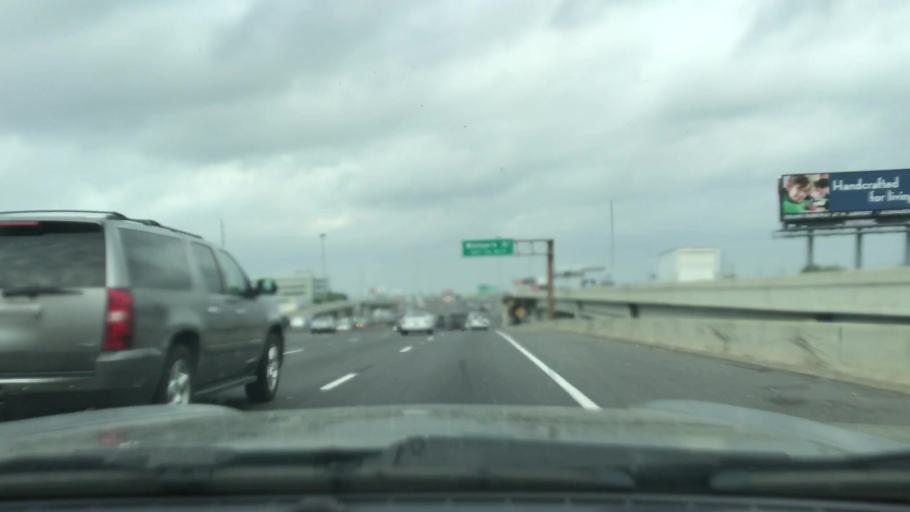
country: US
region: Texas
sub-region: Harris County
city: Bellaire
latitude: 29.7261
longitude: -95.4769
